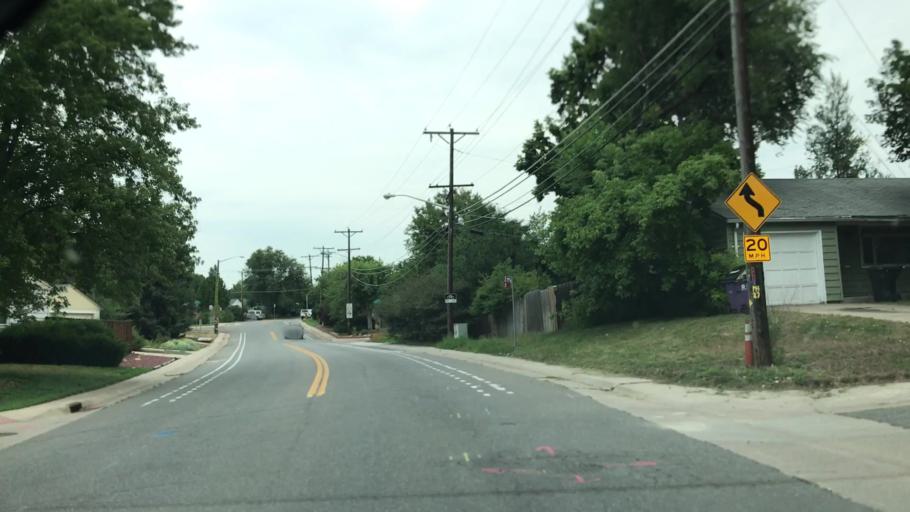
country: US
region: Colorado
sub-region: Arapahoe County
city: Cherry Hills Village
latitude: 39.6670
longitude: -104.9478
